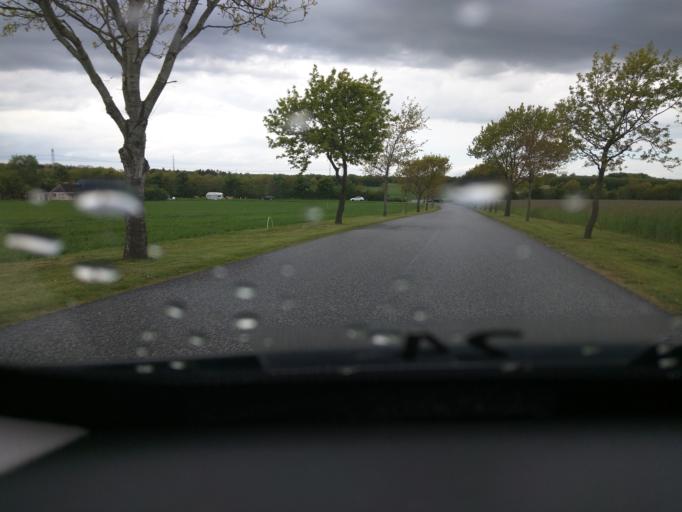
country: DK
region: Central Jutland
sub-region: Viborg Kommune
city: Bjerringbro
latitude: 56.4898
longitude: 9.5769
